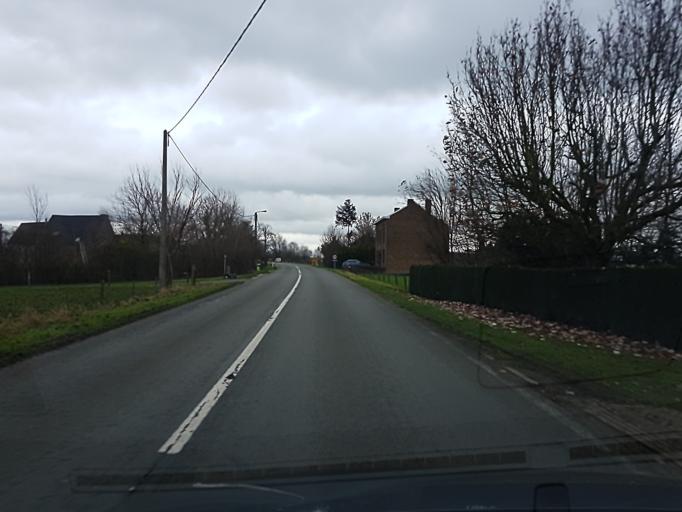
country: BE
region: Wallonia
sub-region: Province de Liege
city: Dalhem
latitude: 50.6950
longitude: 5.7574
